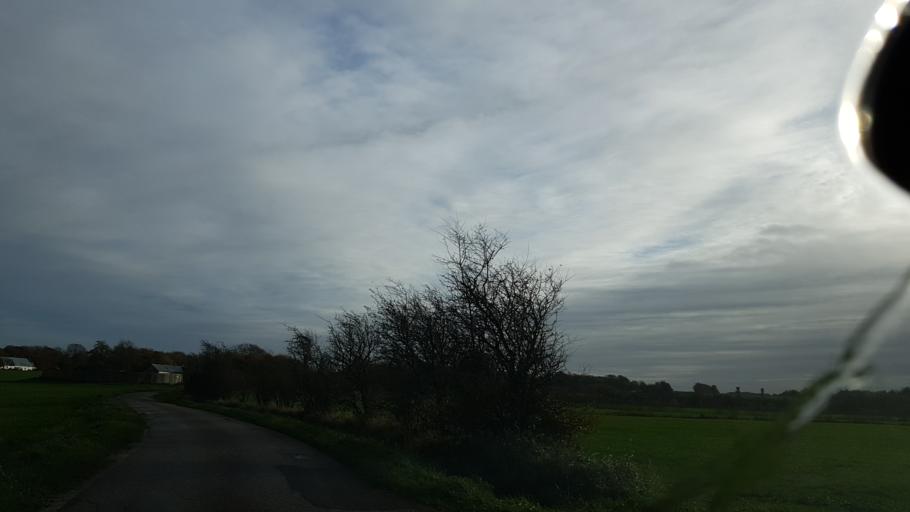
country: DK
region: South Denmark
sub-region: Haderslev Kommune
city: Gram
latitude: 55.2627
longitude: 9.1148
